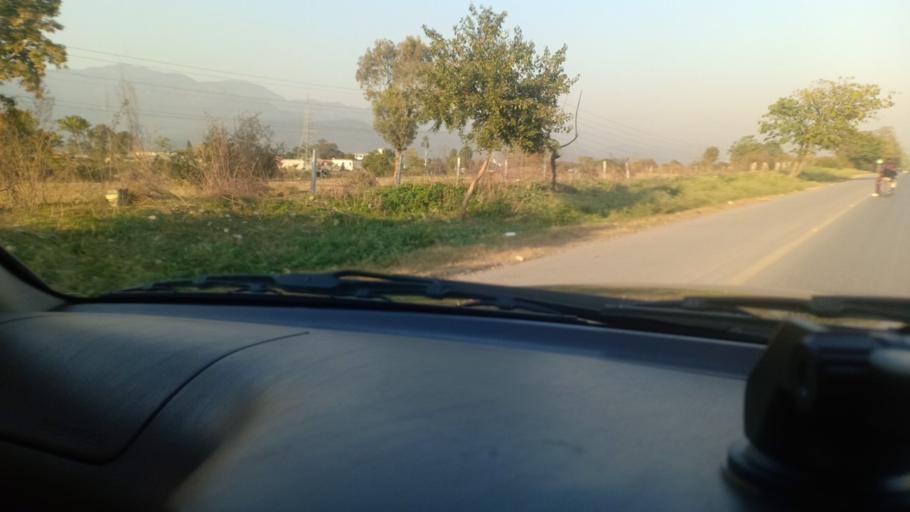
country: PK
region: Islamabad
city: Islamabad
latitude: 33.7275
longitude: 73.1413
